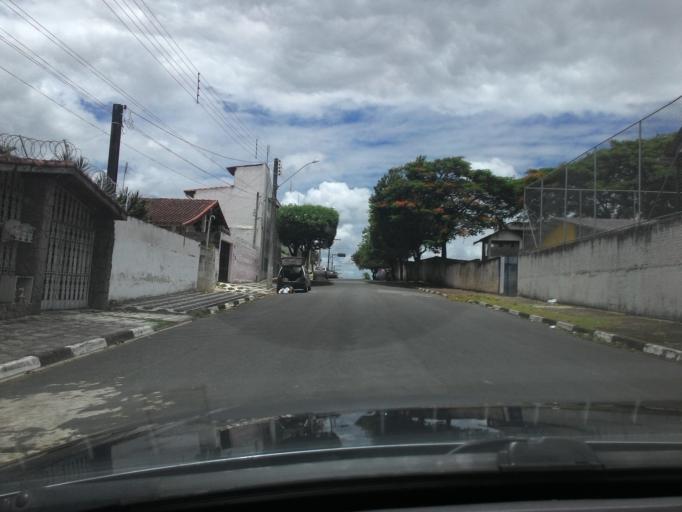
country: BR
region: Sao Paulo
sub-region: Registro
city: Registro
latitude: -24.5048
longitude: -47.8399
